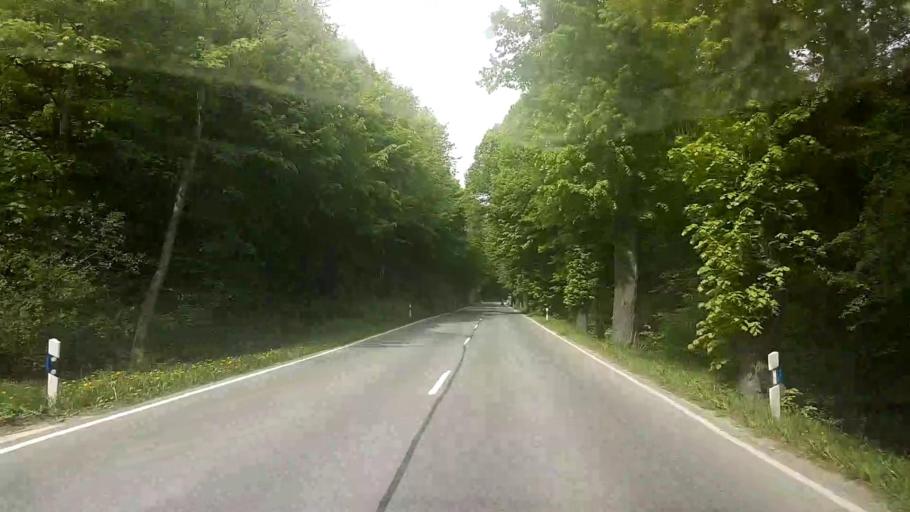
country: DE
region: Bavaria
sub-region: Upper Franconia
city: Lichtenfels
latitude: 50.1626
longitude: 11.0545
